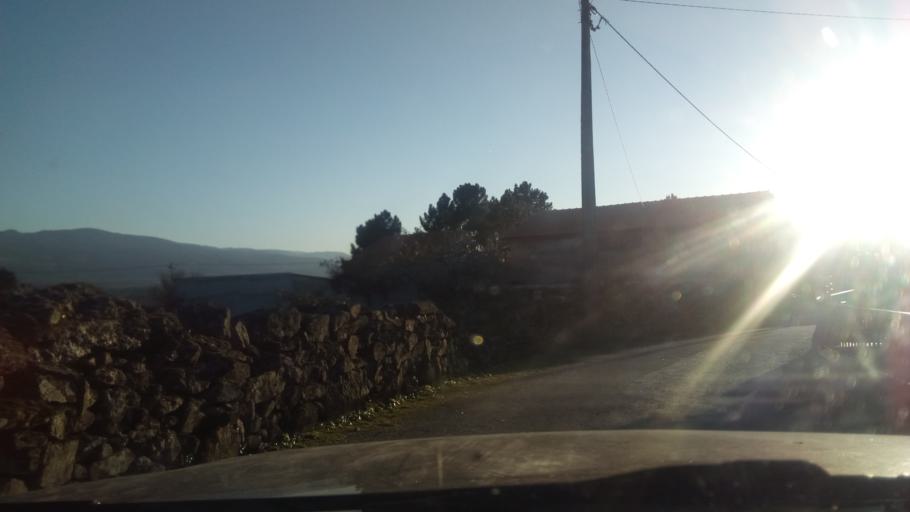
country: PT
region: Guarda
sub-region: Fornos de Algodres
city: Fornos de Algodres
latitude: 40.6052
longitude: -7.5061
